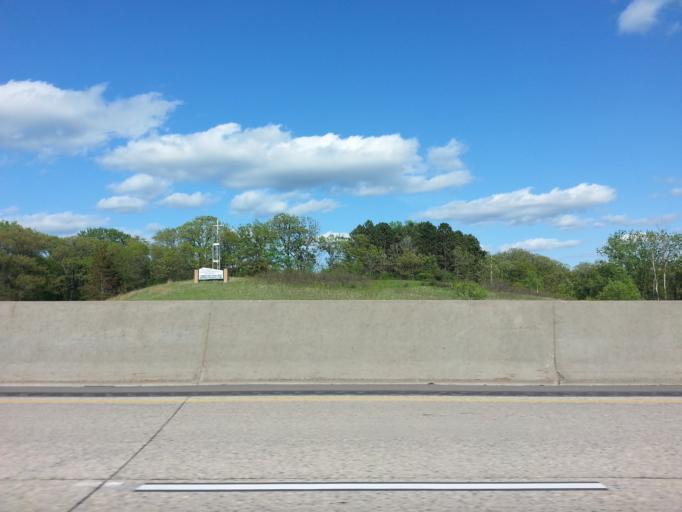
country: US
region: Minnesota
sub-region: Dakota County
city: Burnsville
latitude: 44.7255
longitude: -93.2823
